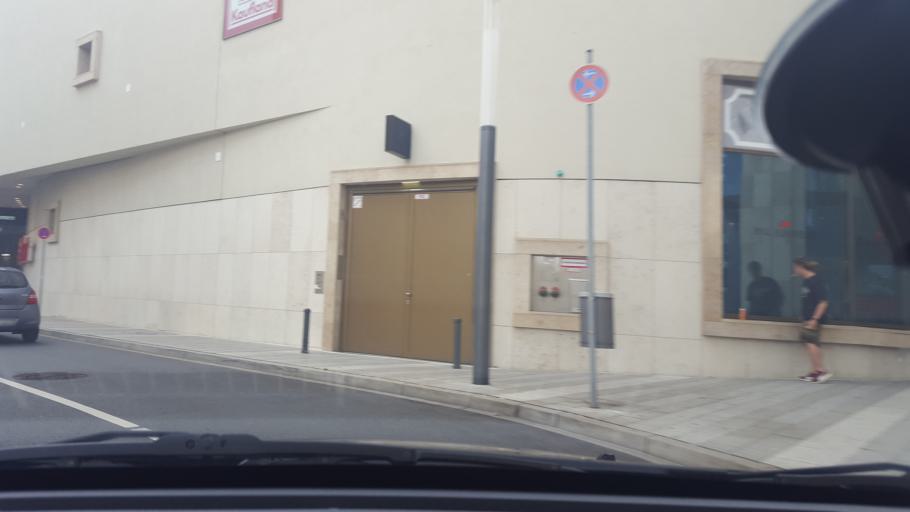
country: DE
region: North Rhine-Westphalia
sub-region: Regierungsbezirk Munster
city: Recklinghausen
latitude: 51.6126
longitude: 7.2000
